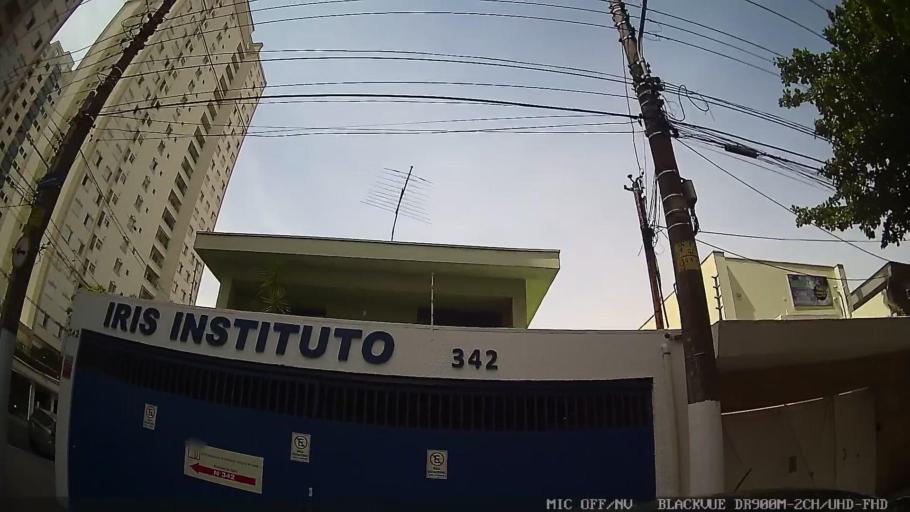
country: BR
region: Sao Paulo
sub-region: Sao Paulo
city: Sao Paulo
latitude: -23.5386
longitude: -46.5739
